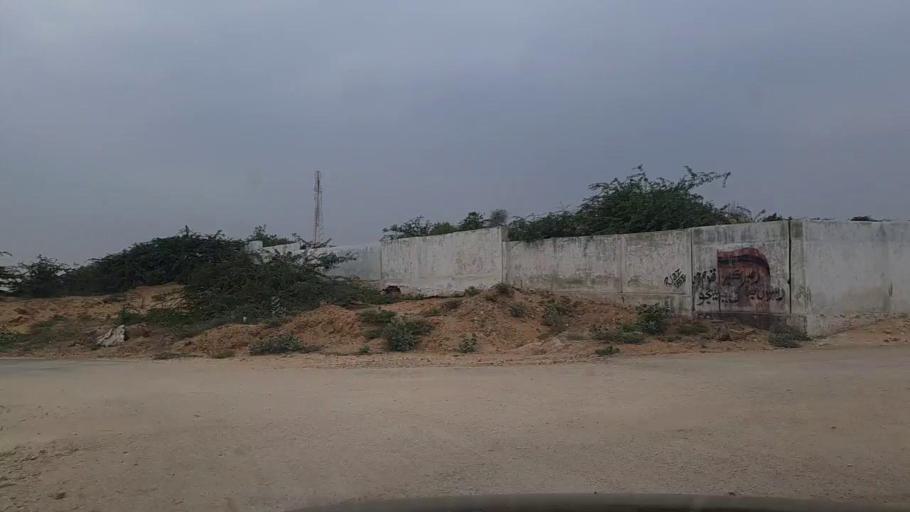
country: PK
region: Sindh
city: Thatta
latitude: 24.8516
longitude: 67.7726
